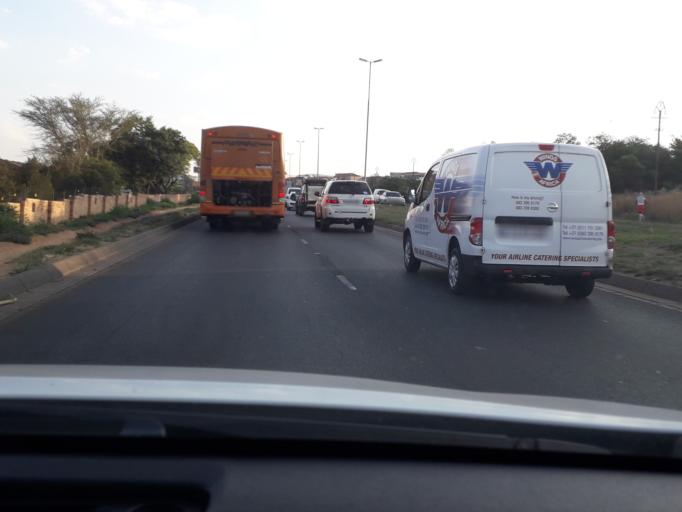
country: ZA
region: Gauteng
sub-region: West Rand District Municipality
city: Muldersdriseloop
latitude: -26.0560
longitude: 27.9553
